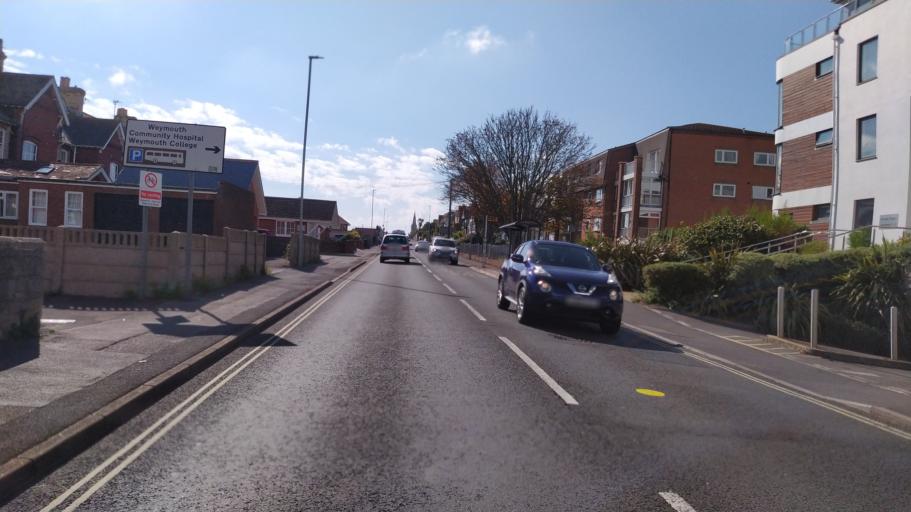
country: GB
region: England
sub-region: Dorset
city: Weymouth
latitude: 50.6238
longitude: -2.4455
